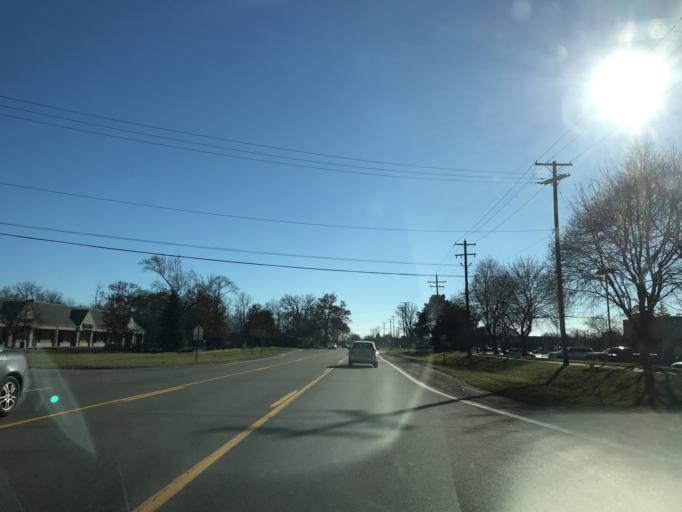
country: US
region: Michigan
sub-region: Oakland County
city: South Lyon
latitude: 42.4450
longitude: -83.6503
